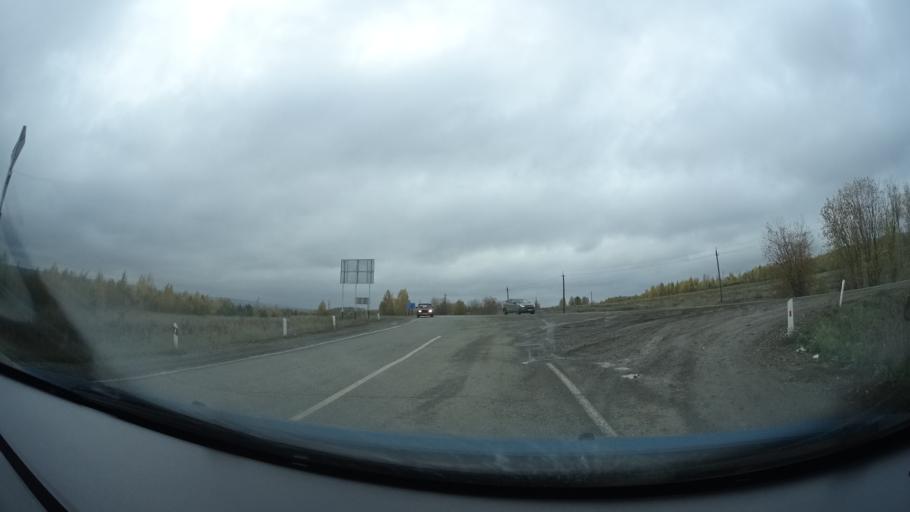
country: RU
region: Perm
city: Osa
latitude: 57.1779
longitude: 55.5317
